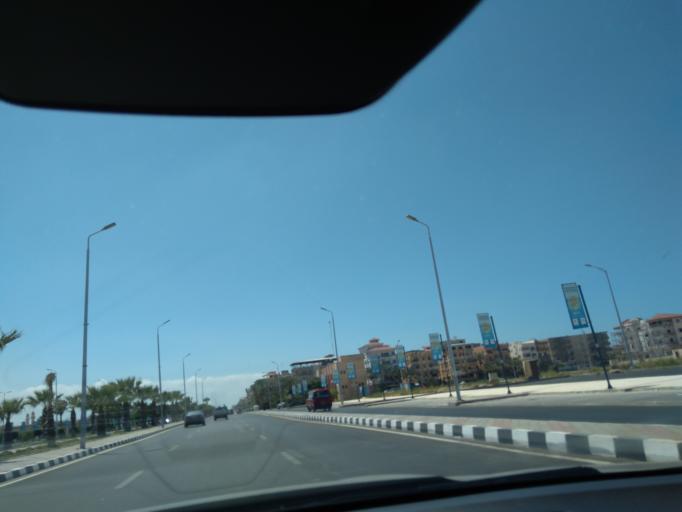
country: EG
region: Dumyat
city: Faraskur
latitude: 31.4433
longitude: 31.6906
